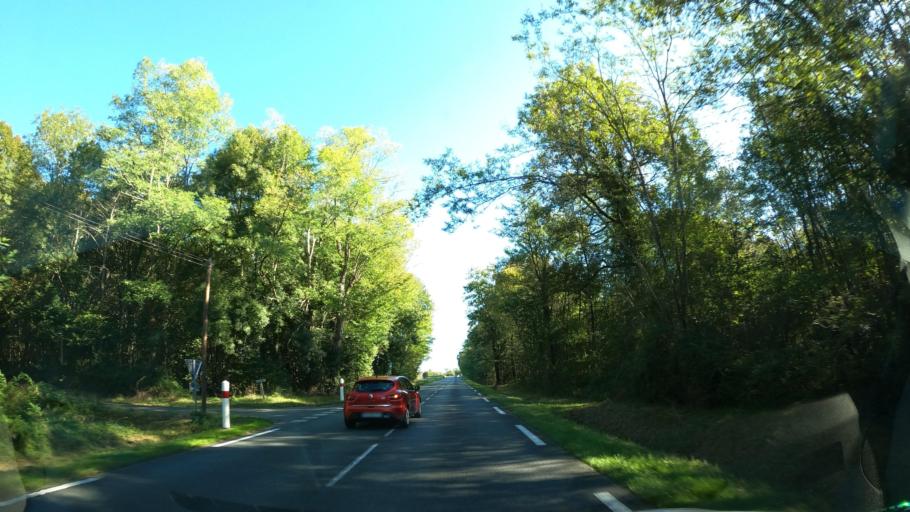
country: FR
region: Aquitaine
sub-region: Departement de la Dordogne
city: Lembras
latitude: 44.9515
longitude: 0.5794
